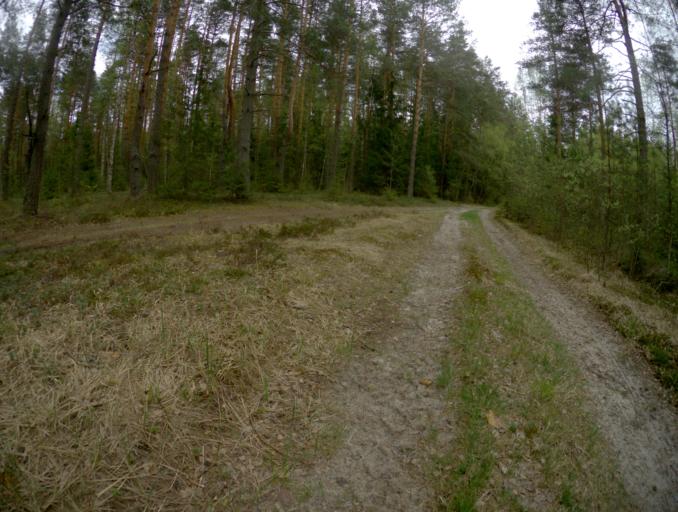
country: RU
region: Vladimir
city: Golovino
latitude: 55.9188
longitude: 40.4098
